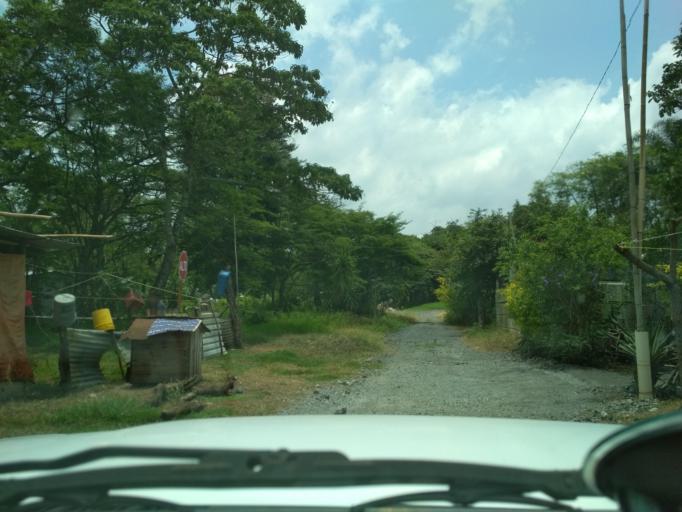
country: MX
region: Veracruz
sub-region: Ixtaczoquitlan
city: Buenavista
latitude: 18.8861
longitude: -97.0630
